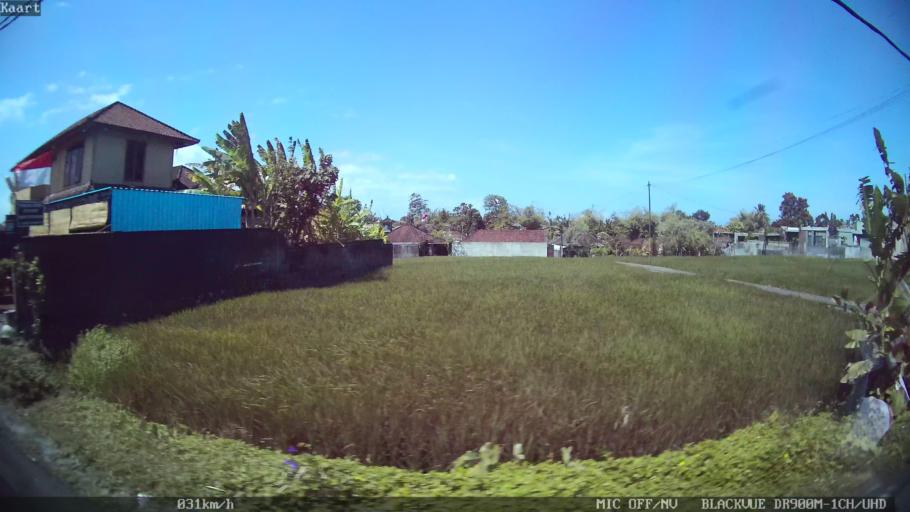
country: ID
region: Bali
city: Denpasar
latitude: -8.6693
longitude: 115.1667
